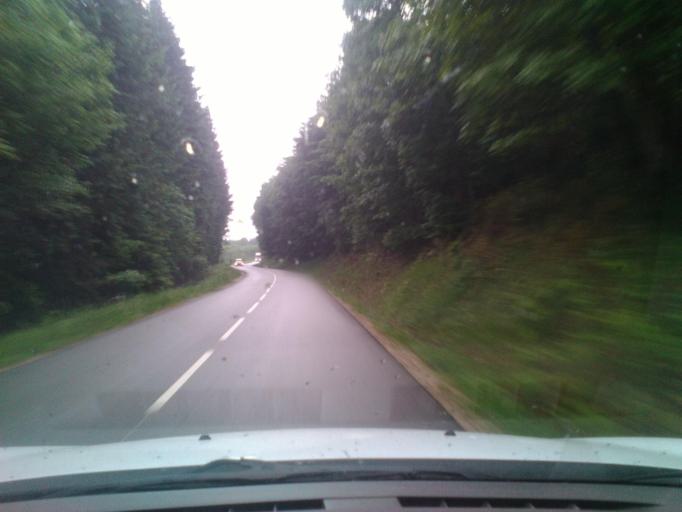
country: FR
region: Lorraine
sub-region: Departement des Vosges
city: Bruyeres
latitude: 48.2565
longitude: 6.7281
